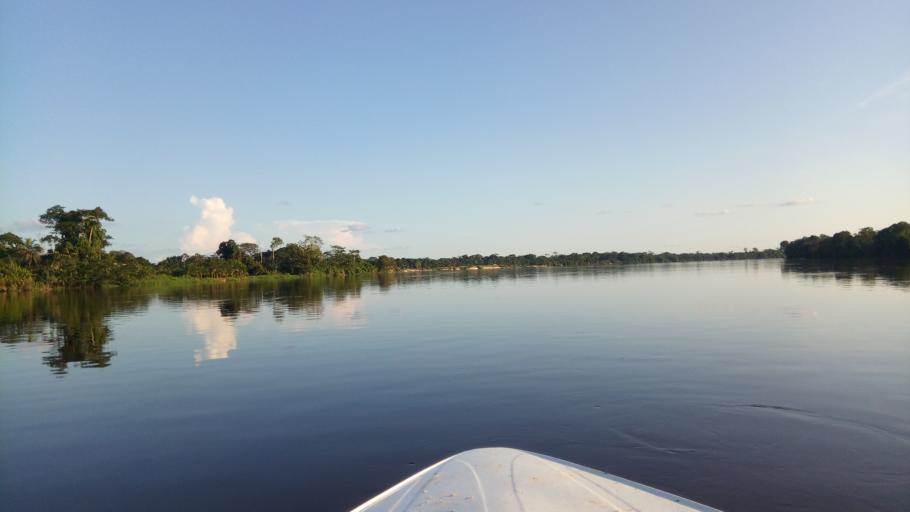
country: CD
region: Eastern Province
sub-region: Sous-Region de la Tshopo
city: Yangambi
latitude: 0.1578
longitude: 24.0522
